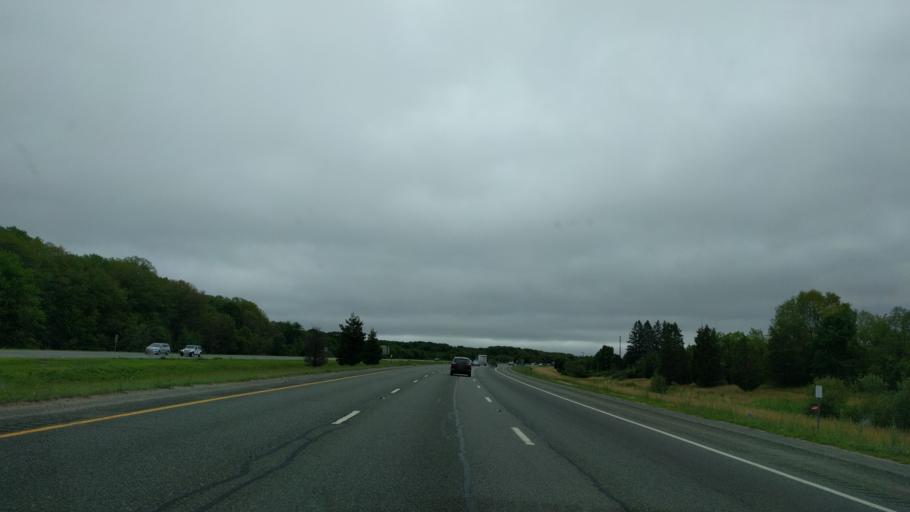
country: US
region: Rhode Island
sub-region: Providence County
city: Johnston
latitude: 41.8551
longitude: -71.5126
